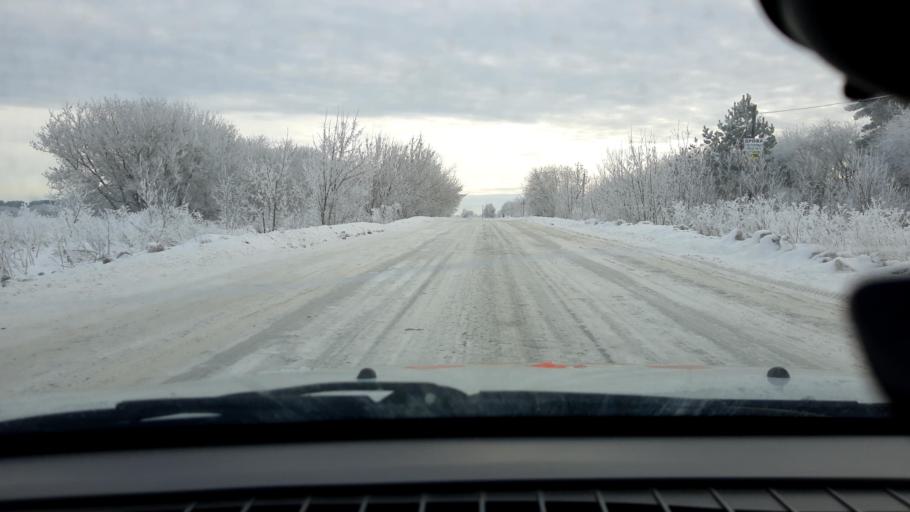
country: RU
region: Nizjnij Novgorod
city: Bogorodsk
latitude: 56.0707
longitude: 43.5793
